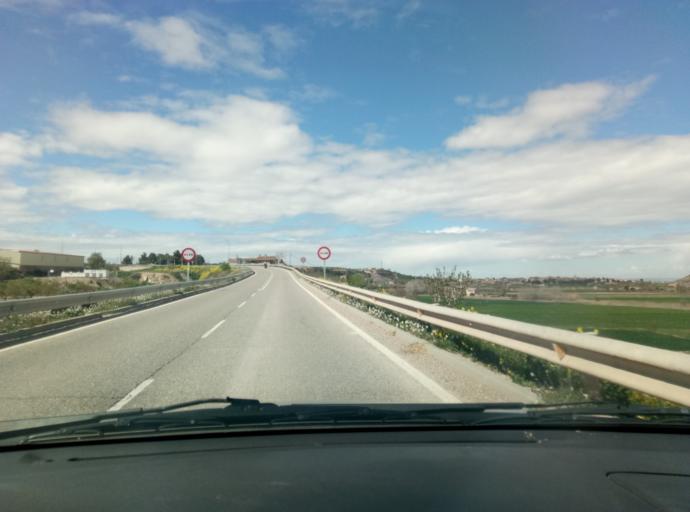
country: ES
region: Catalonia
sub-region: Provincia de Lleida
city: Vallbona de les Monges
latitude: 41.5541
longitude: 1.0390
